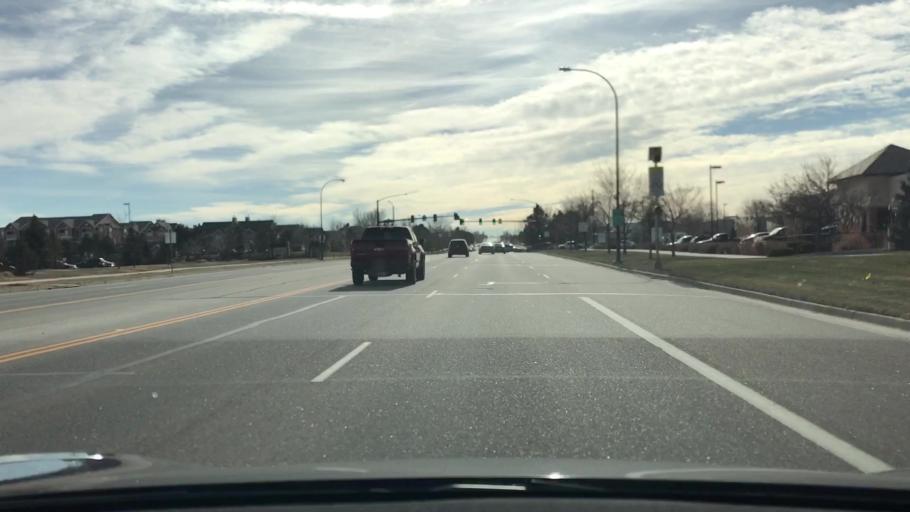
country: US
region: Colorado
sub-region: Adams County
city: Northglenn
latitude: 39.9234
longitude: -104.9969
